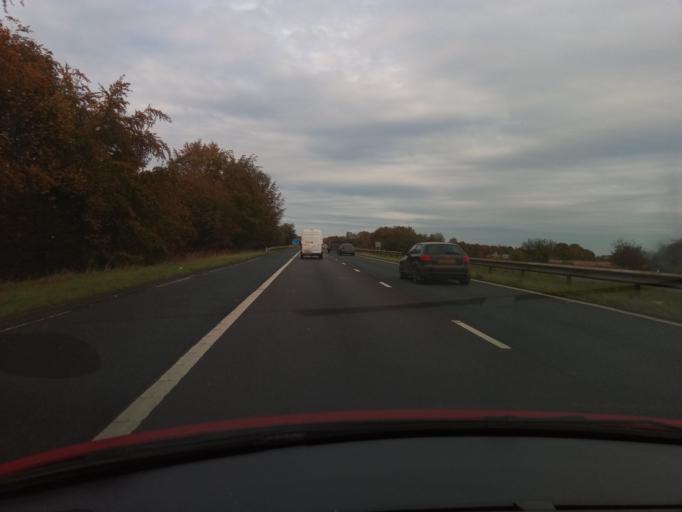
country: GB
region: England
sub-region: Darlington
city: High Coniscliffe
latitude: 54.4987
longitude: -1.6276
